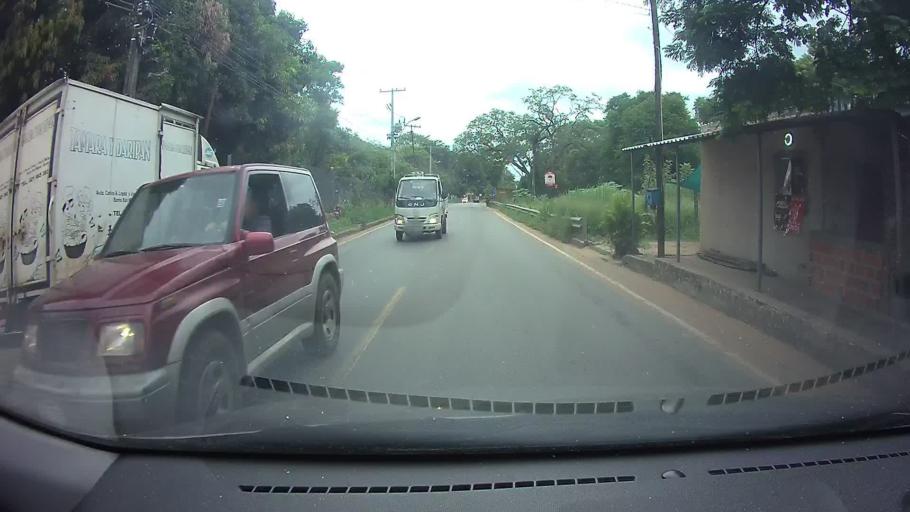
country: PY
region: Central
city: Nemby
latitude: -25.3775
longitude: -57.5453
